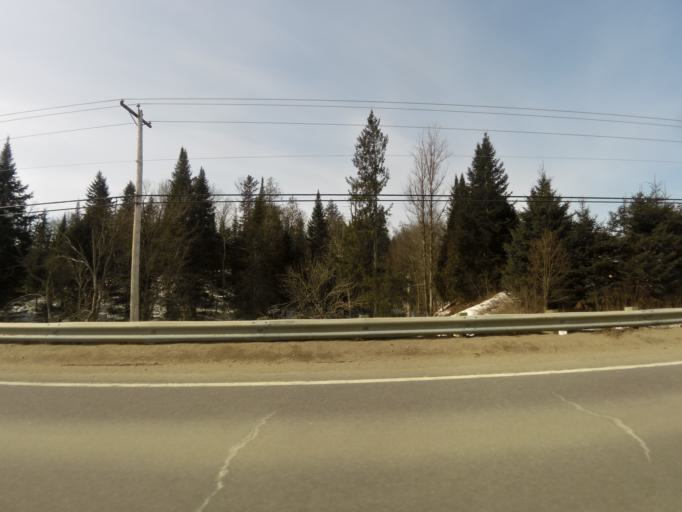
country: CA
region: Quebec
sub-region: Outaouais
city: Val-des-Monts
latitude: 45.6951
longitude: -75.4744
